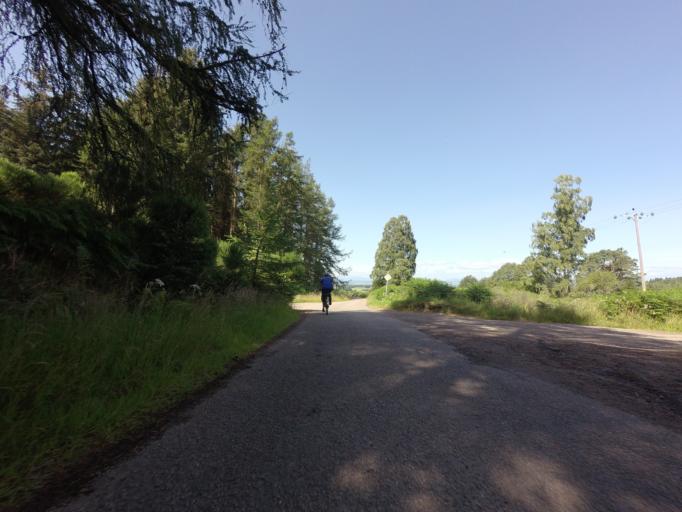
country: GB
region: Scotland
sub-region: Highland
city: Nairn
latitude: 57.5004
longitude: -3.9727
